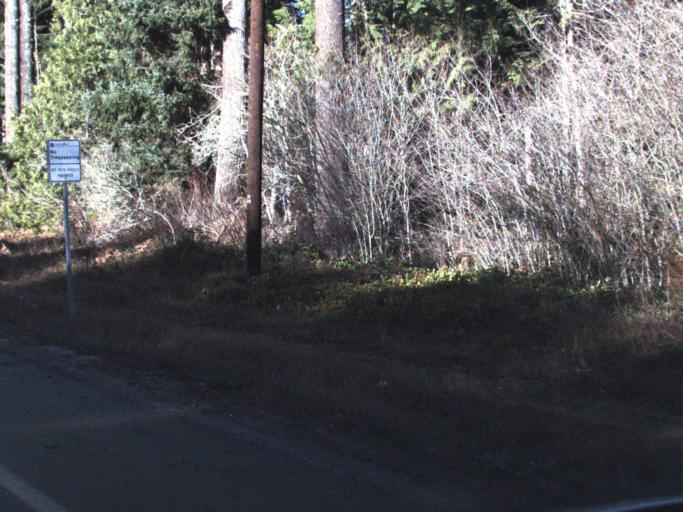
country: US
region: Washington
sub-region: Snohomish County
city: Darrington
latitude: 48.2618
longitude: -121.6249
